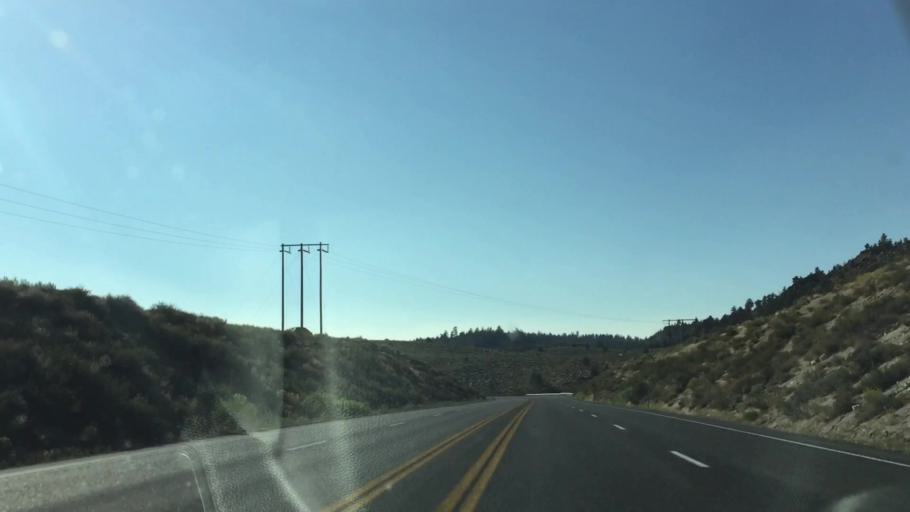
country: US
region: California
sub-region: Inyo County
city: West Bishop
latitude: 37.5561
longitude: -118.6508
